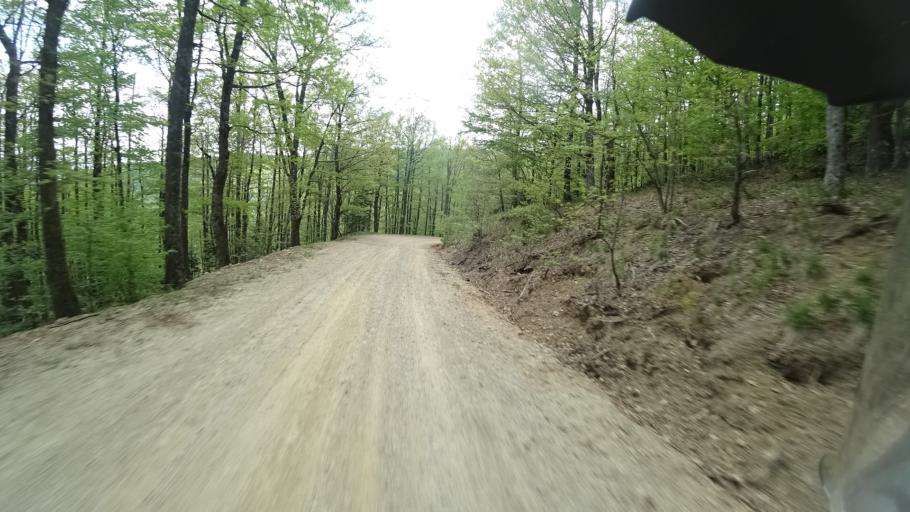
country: HR
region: Grad Zagreb
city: Kasina
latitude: 45.9088
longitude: 15.9927
